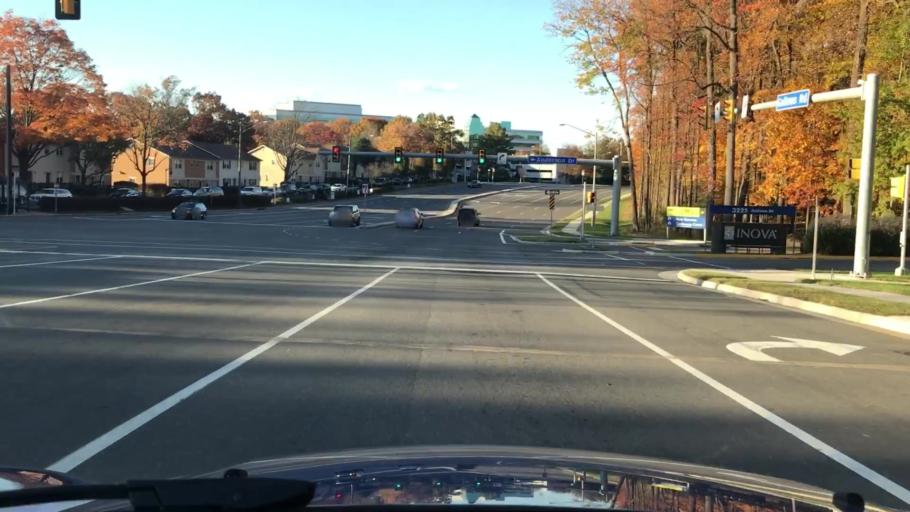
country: US
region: Virginia
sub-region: Fairfax County
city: Merrifield
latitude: 38.8611
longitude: -77.2269
